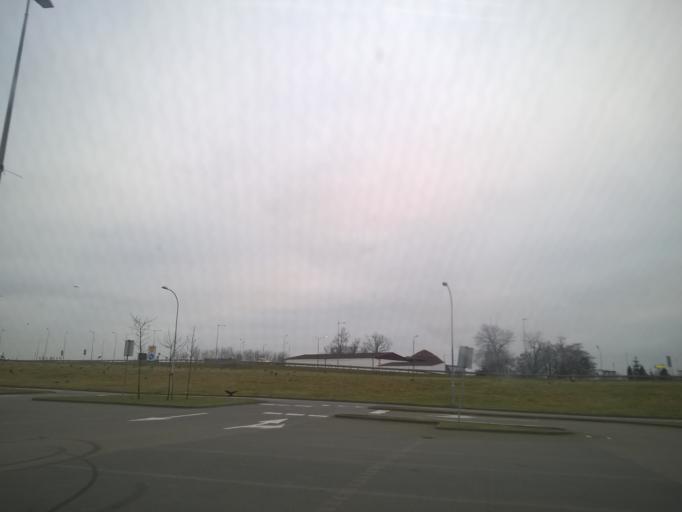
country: PL
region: Lower Silesian Voivodeship
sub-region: Powiat wroclawski
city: Bielany Wroclawskie
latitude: 51.0517
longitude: 16.9714
